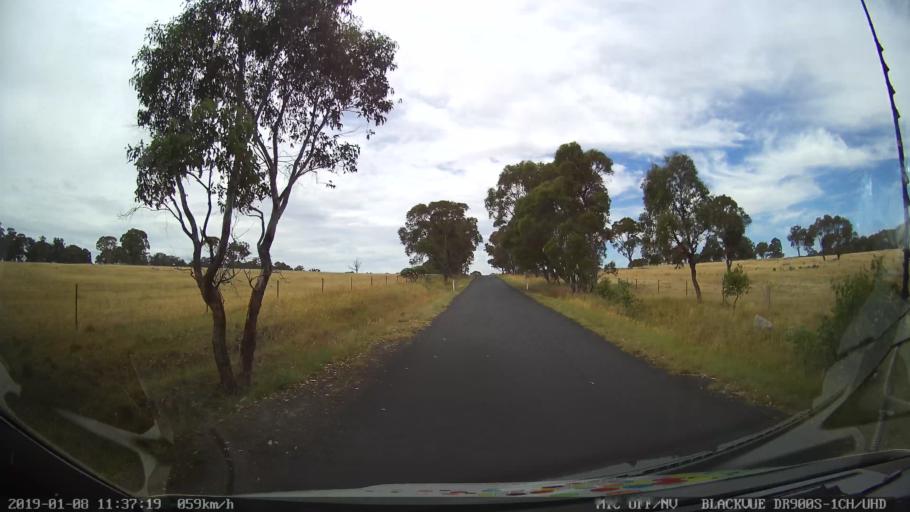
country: AU
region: New South Wales
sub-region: Guyra
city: Guyra
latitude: -30.3513
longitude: 151.5508
